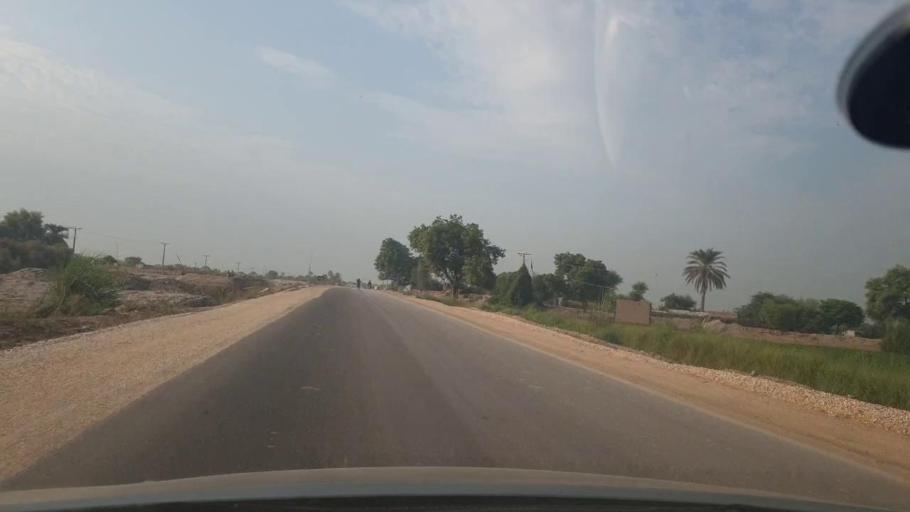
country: PK
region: Sindh
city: Jacobabad
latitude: 28.1995
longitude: 68.3678
